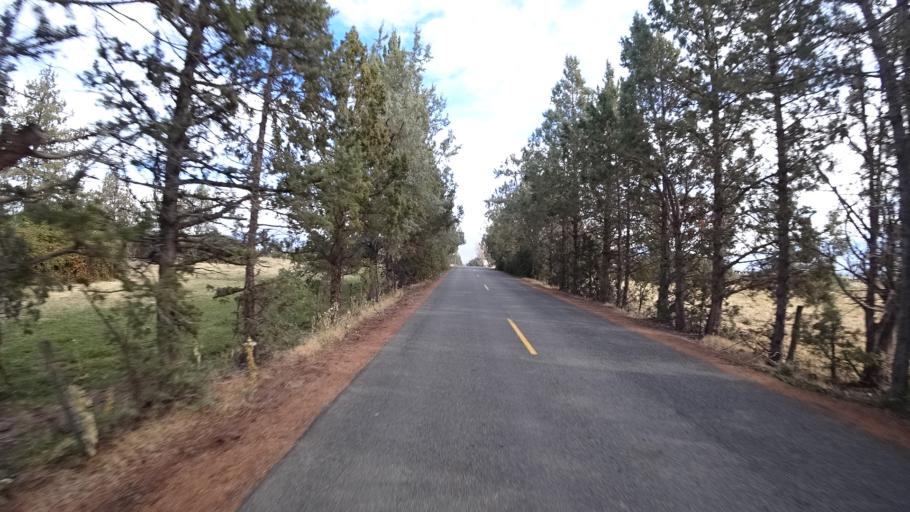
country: US
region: California
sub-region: Siskiyou County
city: Montague
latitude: 41.6385
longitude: -122.4226
